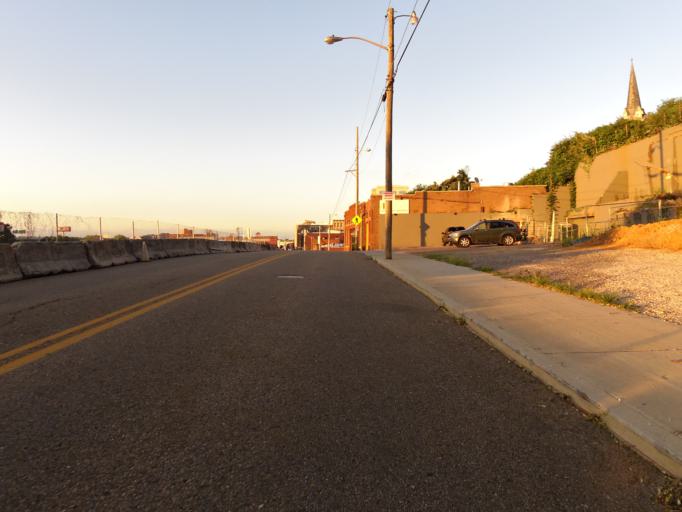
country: US
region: Tennessee
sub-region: Knox County
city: Knoxville
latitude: 35.9670
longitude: -83.9235
